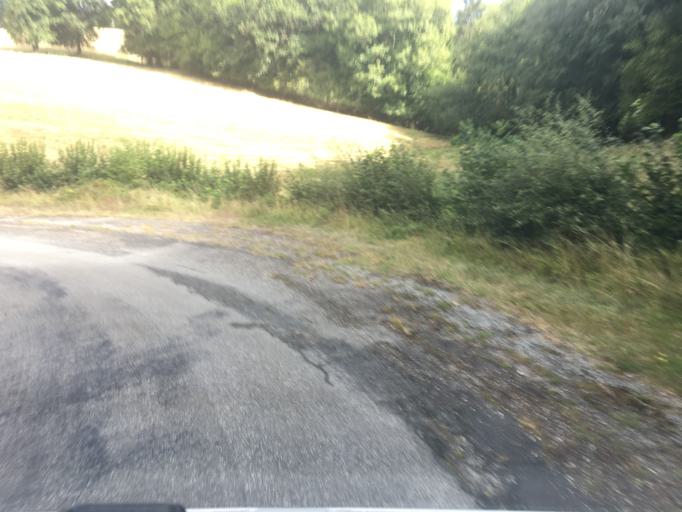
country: FR
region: Auvergne
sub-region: Departement du Cantal
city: Champagnac
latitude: 45.4406
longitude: 2.4012
